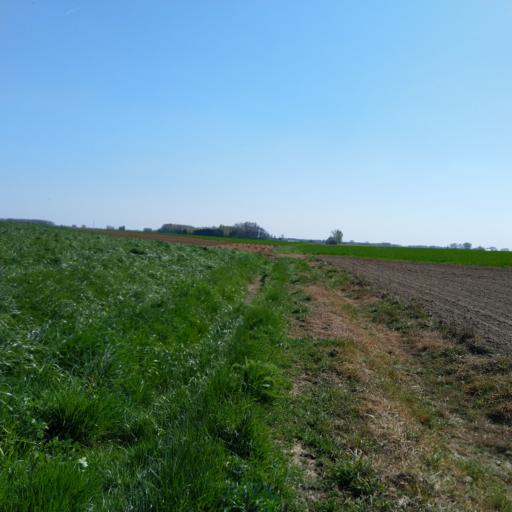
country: BE
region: Wallonia
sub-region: Province du Hainaut
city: Jurbise
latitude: 50.5541
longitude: 3.9370
